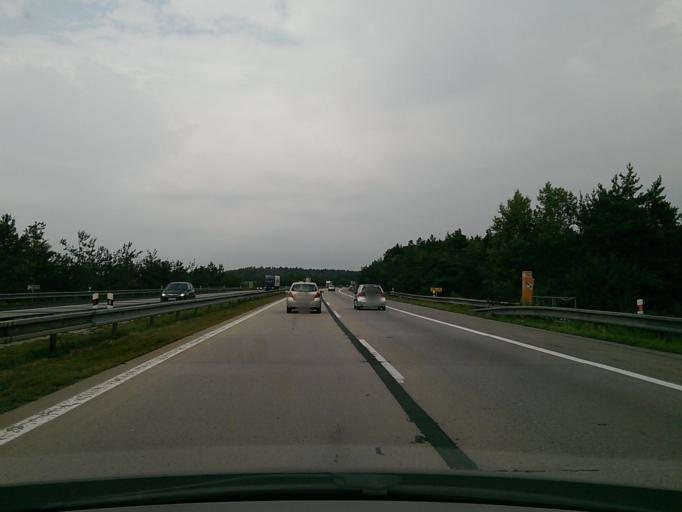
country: CZ
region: South Moravian
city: Ricany
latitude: 49.2348
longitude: 16.3774
